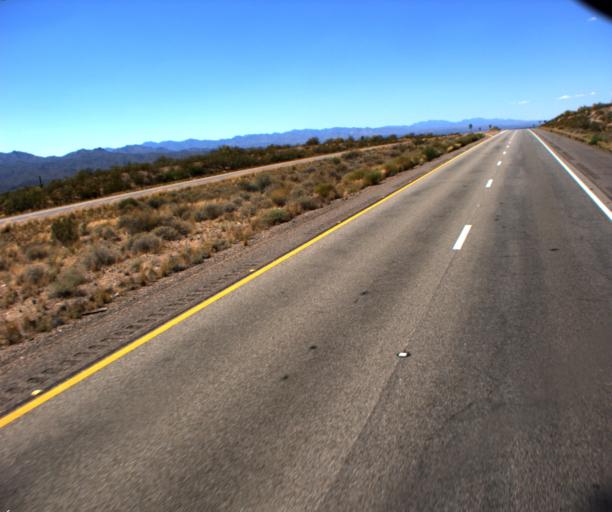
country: US
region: Arizona
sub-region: Yavapai County
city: Bagdad
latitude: 34.6070
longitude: -113.5226
